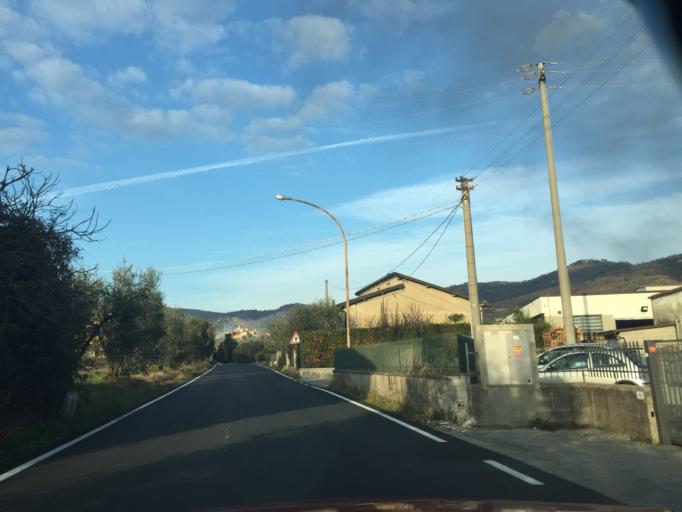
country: IT
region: Tuscany
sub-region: Provincia di Pistoia
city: San Rocco
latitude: 43.8367
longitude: 10.8675
